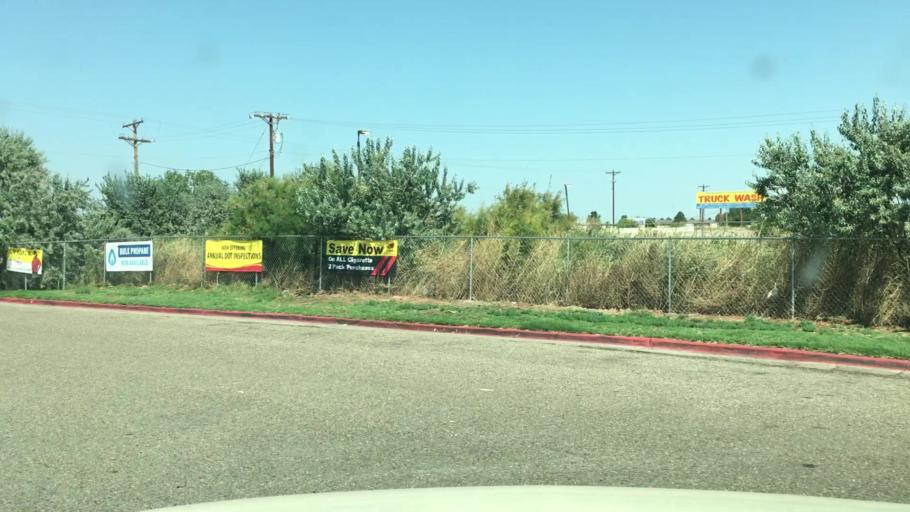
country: US
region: New Mexico
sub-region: Quay County
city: Tucumcari
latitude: 35.1594
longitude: -103.7015
